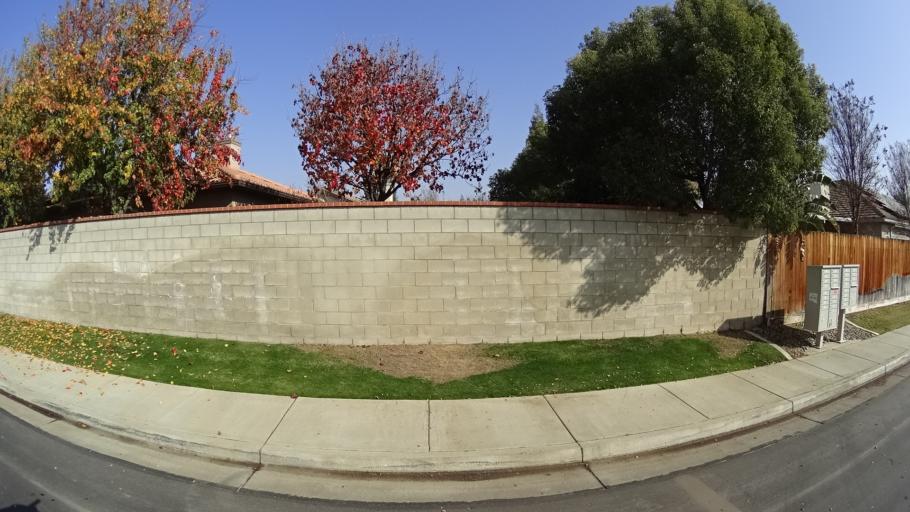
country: US
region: California
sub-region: Kern County
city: Greenacres
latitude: 35.4174
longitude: -119.1141
